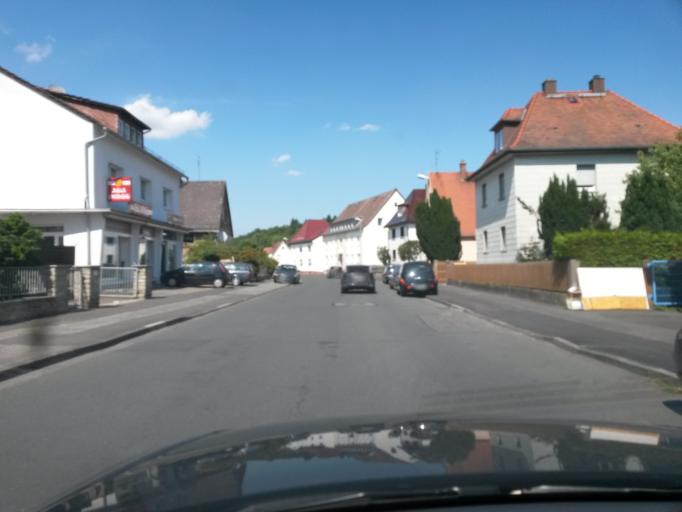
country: DE
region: Hesse
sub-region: Regierungsbezirk Darmstadt
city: Neu-Anspach
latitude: 50.2966
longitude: 8.5154
